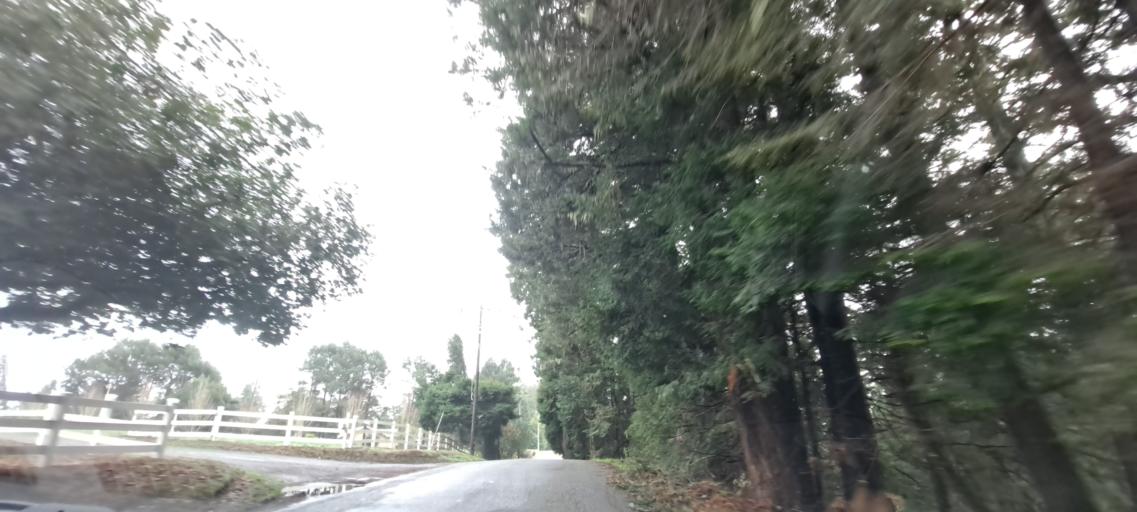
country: US
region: California
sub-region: Humboldt County
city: Fortuna
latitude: 40.6029
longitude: -124.1401
